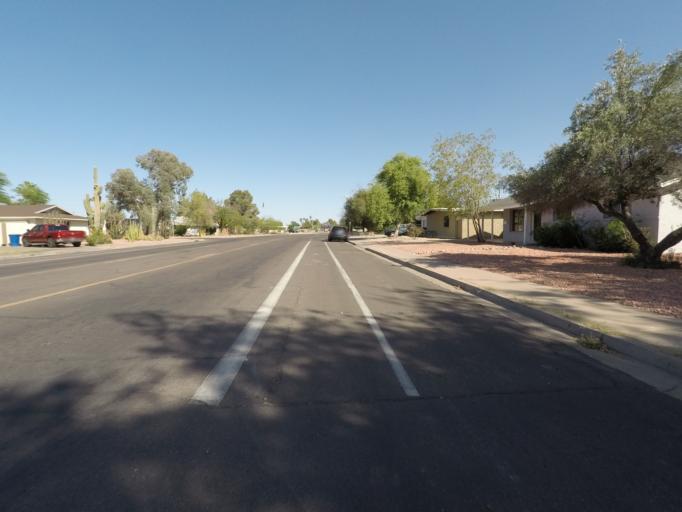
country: US
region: Arizona
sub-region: Maricopa County
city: Tempe
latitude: 33.4025
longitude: -111.9167
